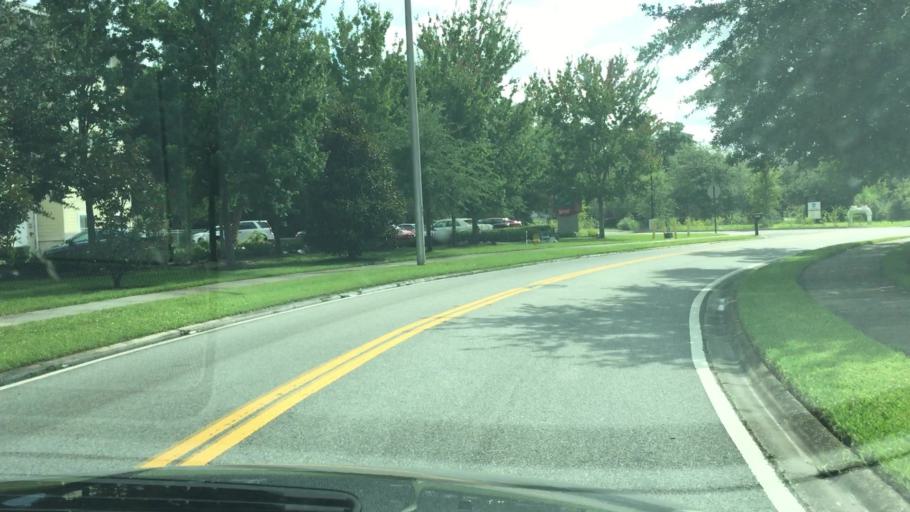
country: US
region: Florida
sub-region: Duval County
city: Jacksonville
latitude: 30.2498
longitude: -81.5988
